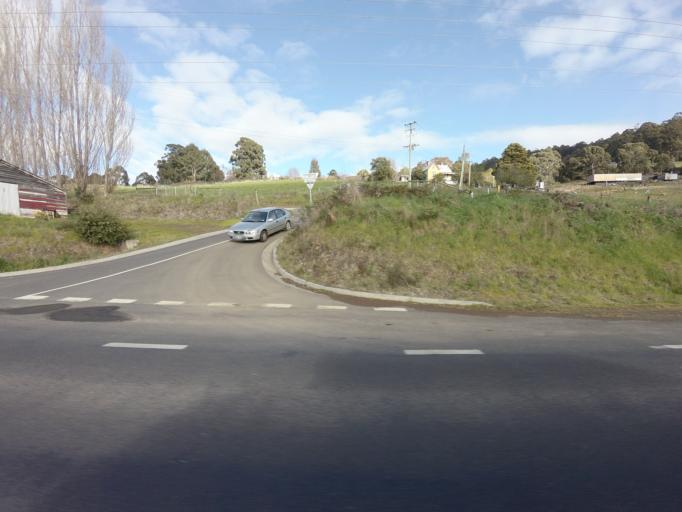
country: AU
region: Tasmania
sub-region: Huon Valley
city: Franklin
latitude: -43.1072
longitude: 147.0006
